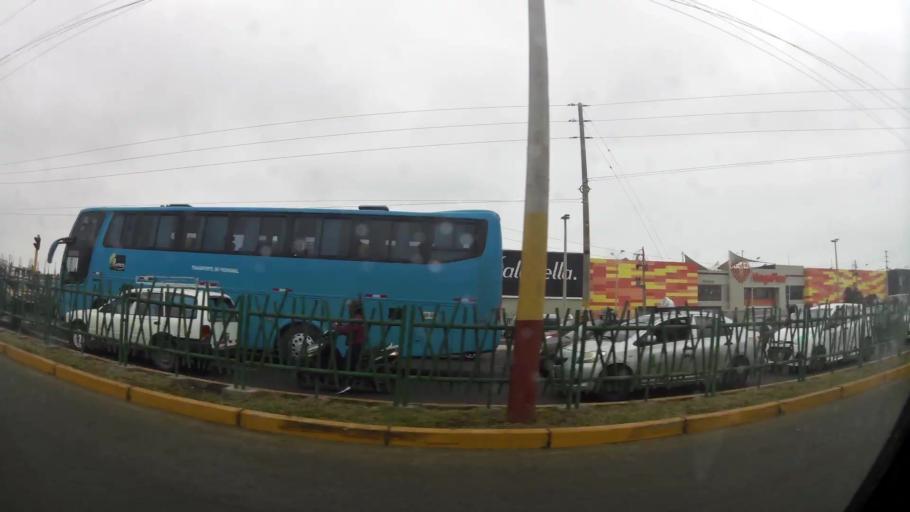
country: PE
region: Ancash
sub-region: Provincia de Santa
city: Chimbote
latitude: -9.1019
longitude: -78.5562
